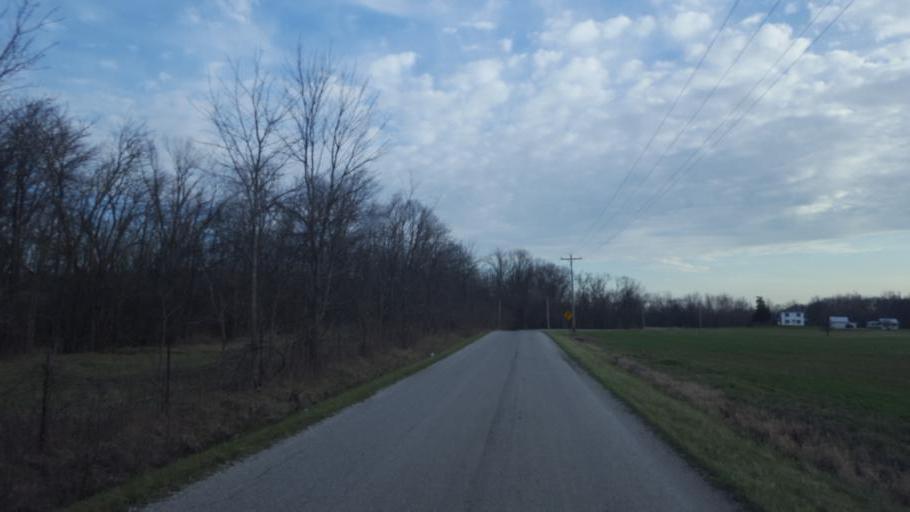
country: US
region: Ohio
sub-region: Crawford County
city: Bucyrus
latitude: 40.6638
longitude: -82.9483
